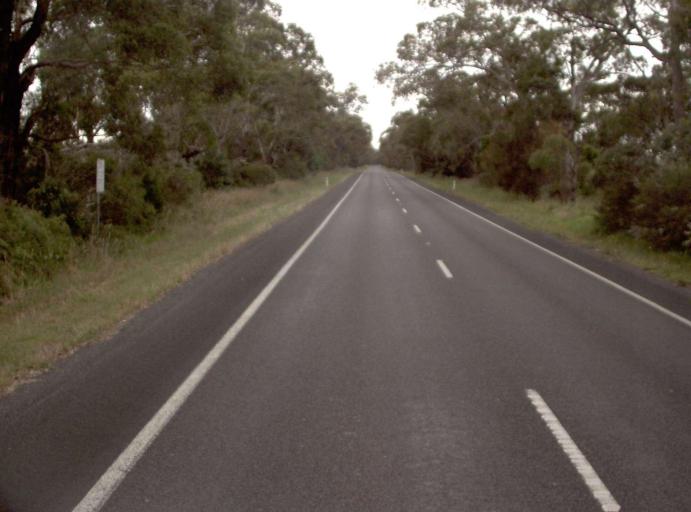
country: AU
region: Victoria
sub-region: Latrobe
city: Traralgon
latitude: -38.5487
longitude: 146.8257
